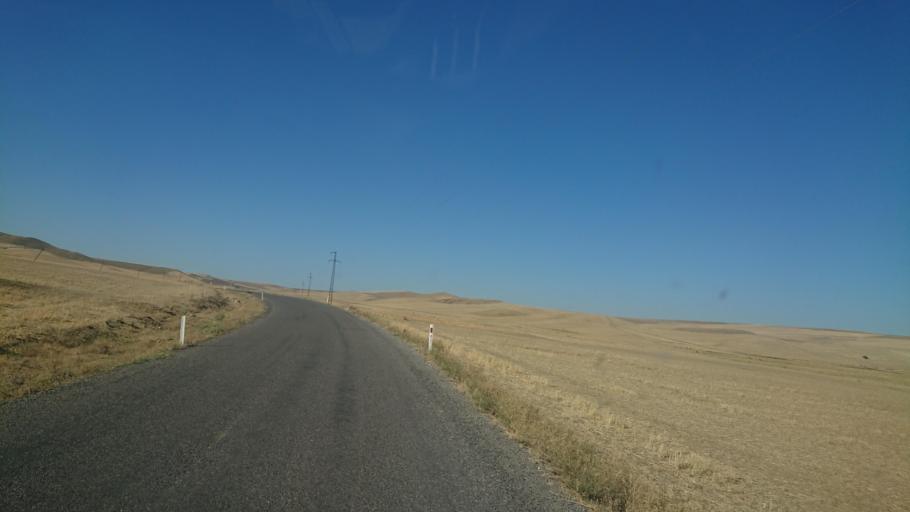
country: TR
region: Aksaray
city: Agacoren
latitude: 38.7778
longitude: 33.7089
